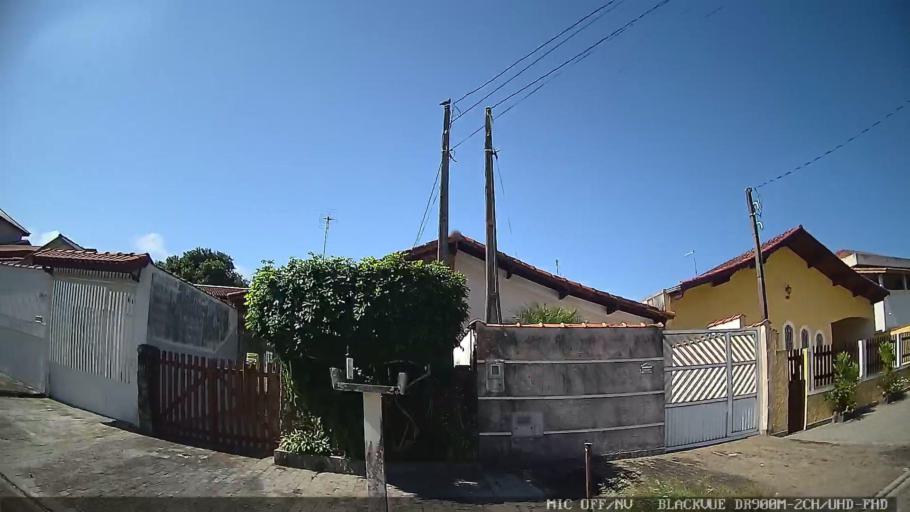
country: BR
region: Sao Paulo
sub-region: Peruibe
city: Peruibe
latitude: -24.3119
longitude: -46.9982
